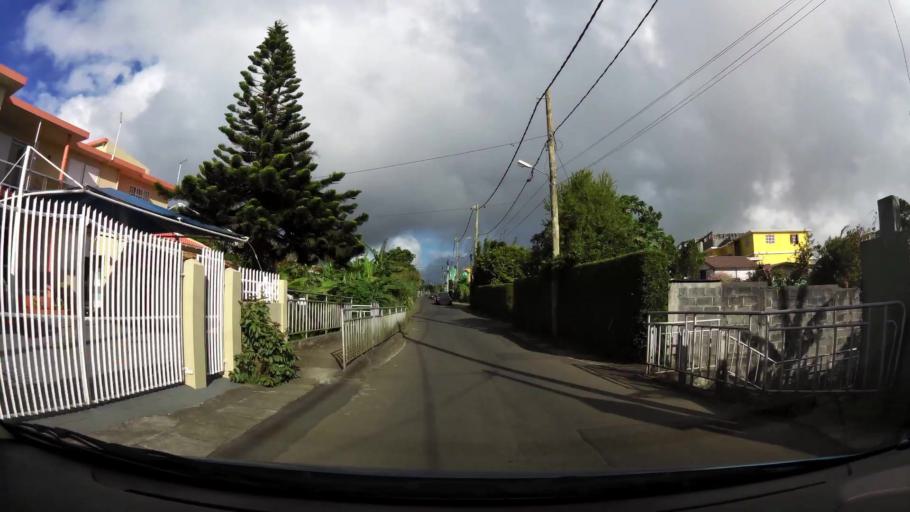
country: MU
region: Plaines Wilhems
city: Curepipe
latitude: -20.3263
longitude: 57.5066
